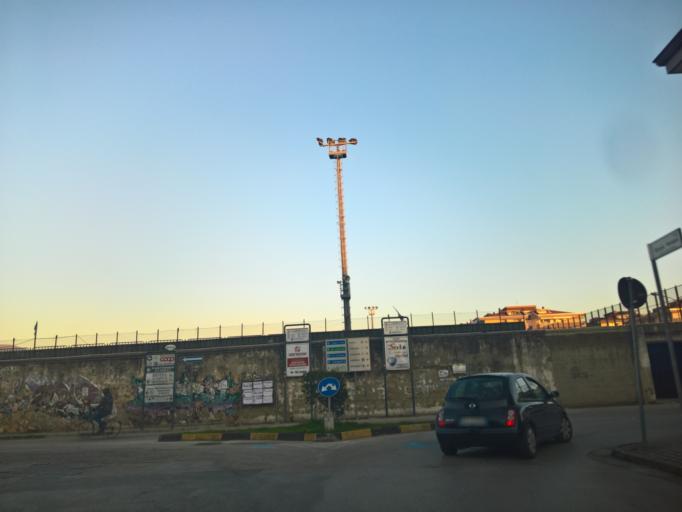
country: IT
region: Campania
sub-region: Provincia di Caserta
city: Santa Maria Capua Vetere
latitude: 41.0884
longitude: 14.2560
